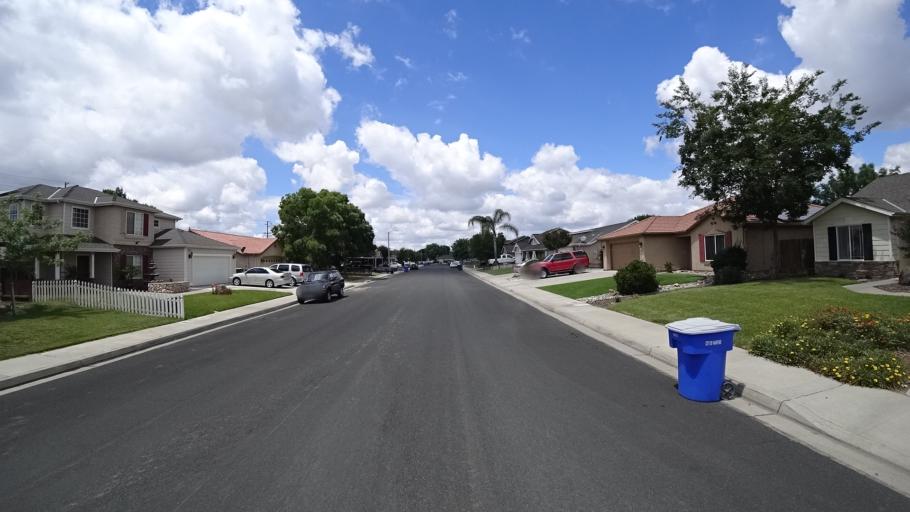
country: US
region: California
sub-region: Kings County
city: Hanford
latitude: 36.3431
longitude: -119.6255
